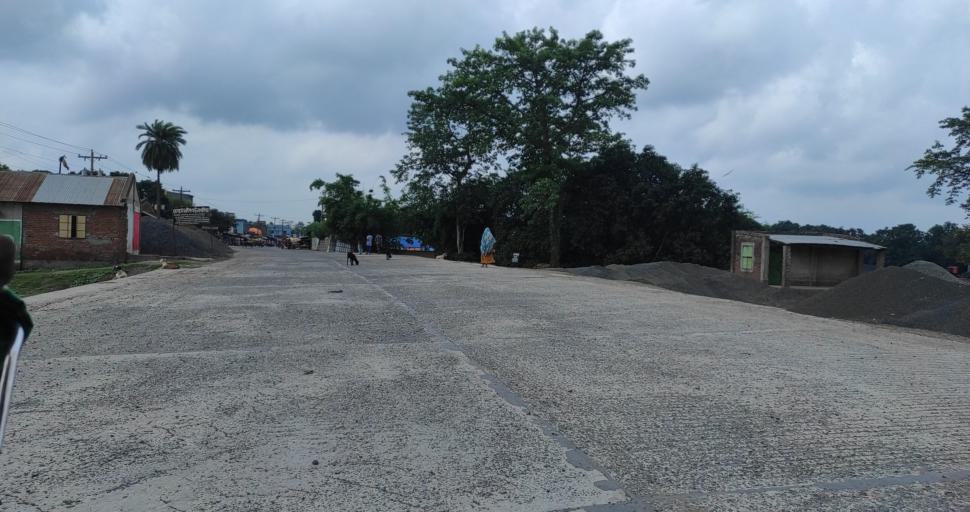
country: BD
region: Rajshahi
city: Shibganj
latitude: 24.8374
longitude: 88.1417
